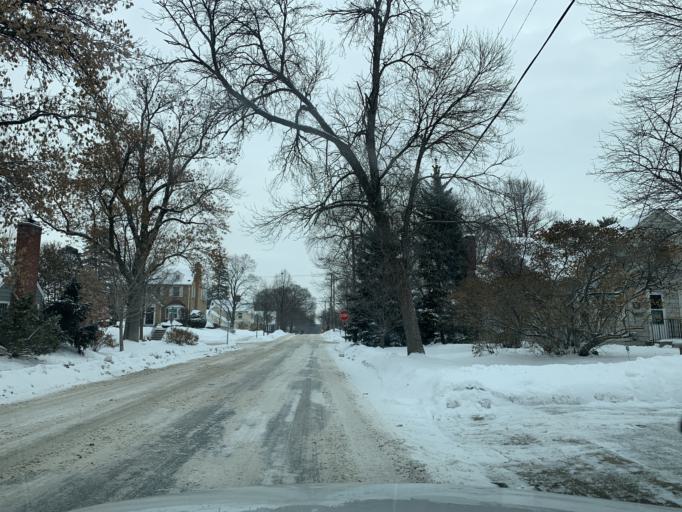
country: US
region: Minnesota
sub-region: Hennepin County
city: Saint Louis Park
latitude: 44.9324
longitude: -93.3361
